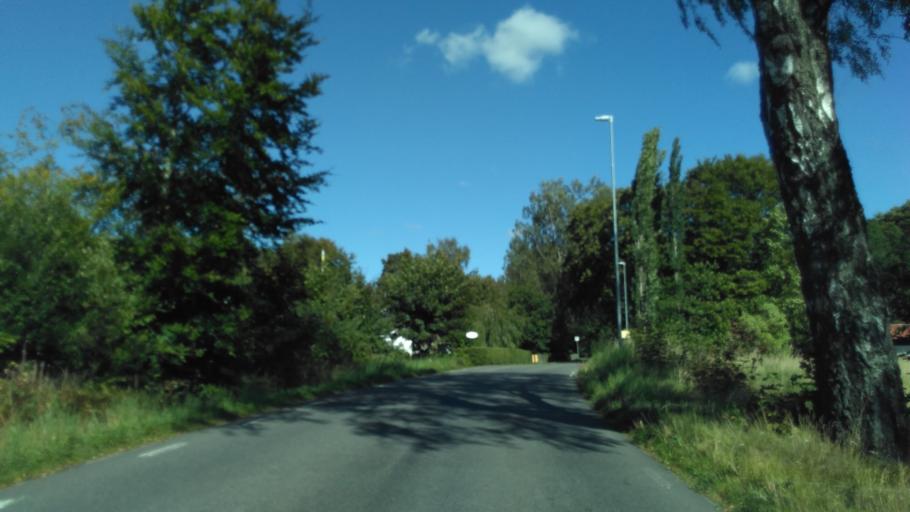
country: SE
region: Vaestra Goetaland
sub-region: Skara Kommun
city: Axvall
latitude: 58.4174
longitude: 13.6113
